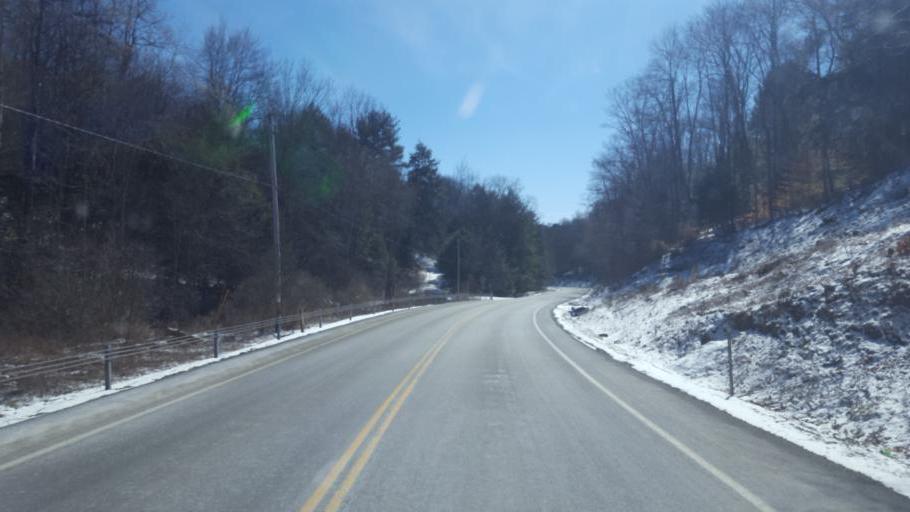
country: US
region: New York
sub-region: Allegany County
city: Andover
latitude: 42.0506
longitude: -77.7923
